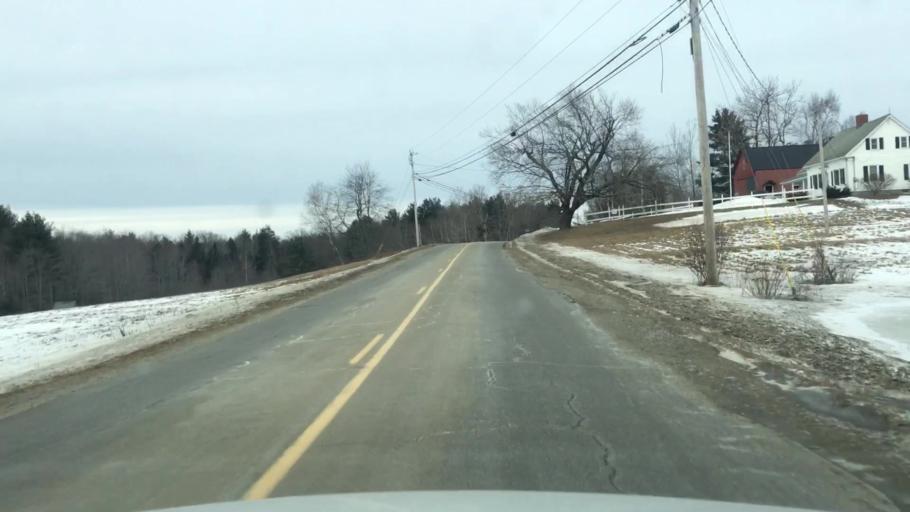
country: US
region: Maine
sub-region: Kennebec County
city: Chelsea
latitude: 44.2656
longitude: -69.6496
